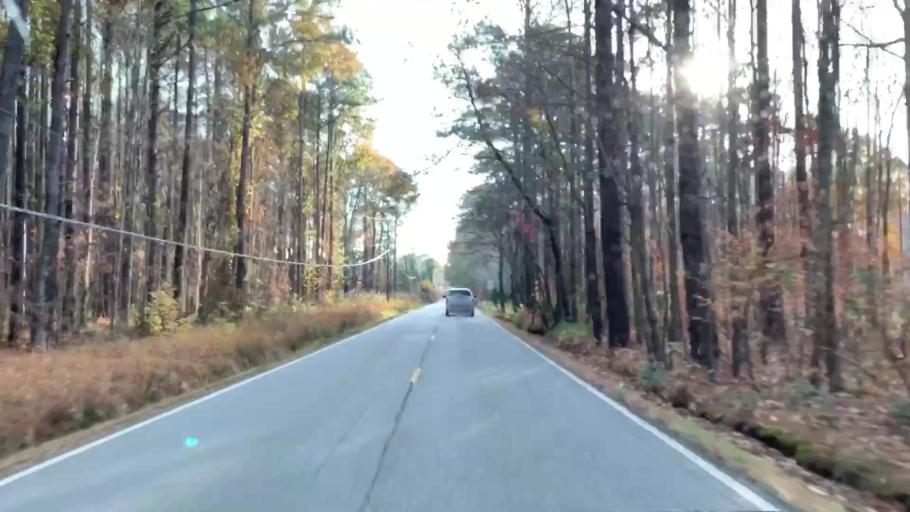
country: US
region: Virginia
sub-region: City of Virginia Beach
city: Virginia Beach
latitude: 36.7388
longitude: -76.1068
